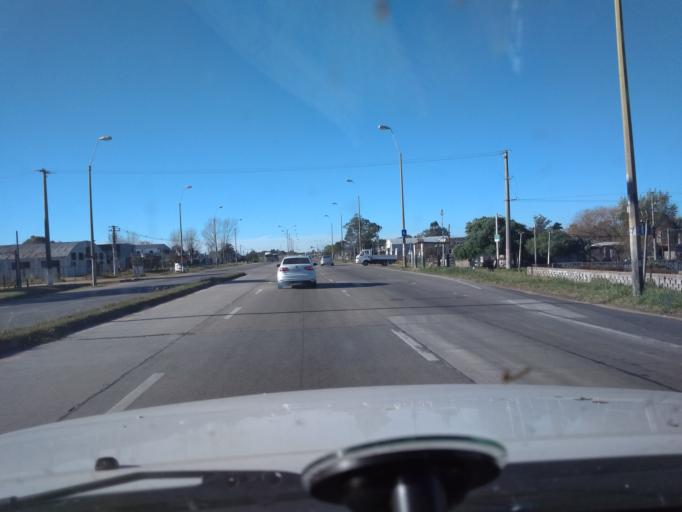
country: UY
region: Canelones
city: Colonia Nicolich
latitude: -34.7788
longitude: -56.0566
